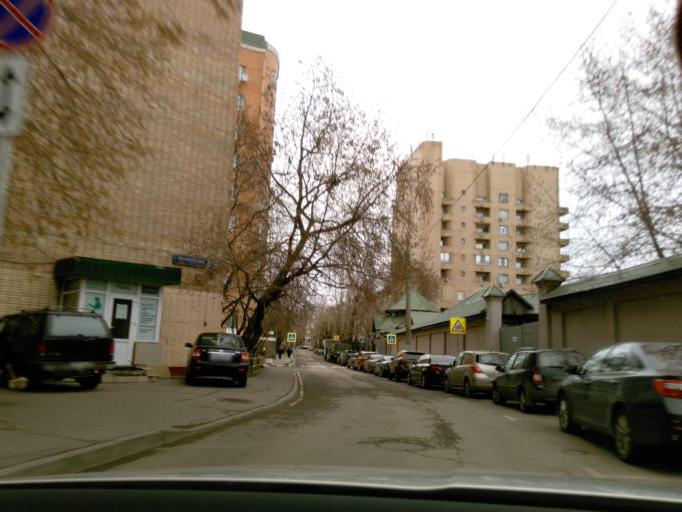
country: RU
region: Moskovskaya
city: Dorogomilovo
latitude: 55.7644
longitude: 37.5826
